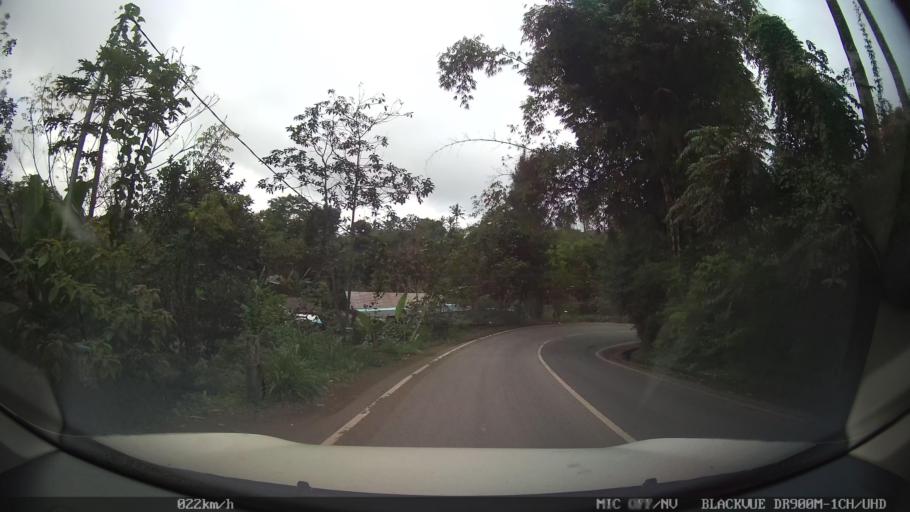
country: ID
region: Bali
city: Banjar Geriana Kangin
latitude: -8.3820
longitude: 115.4446
